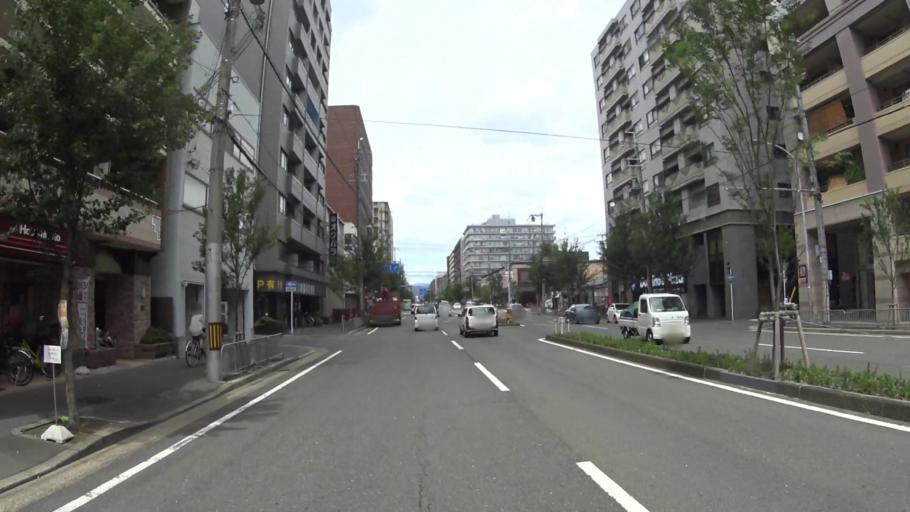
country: JP
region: Kyoto
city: Kyoto
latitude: 34.9917
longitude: 135.7323
